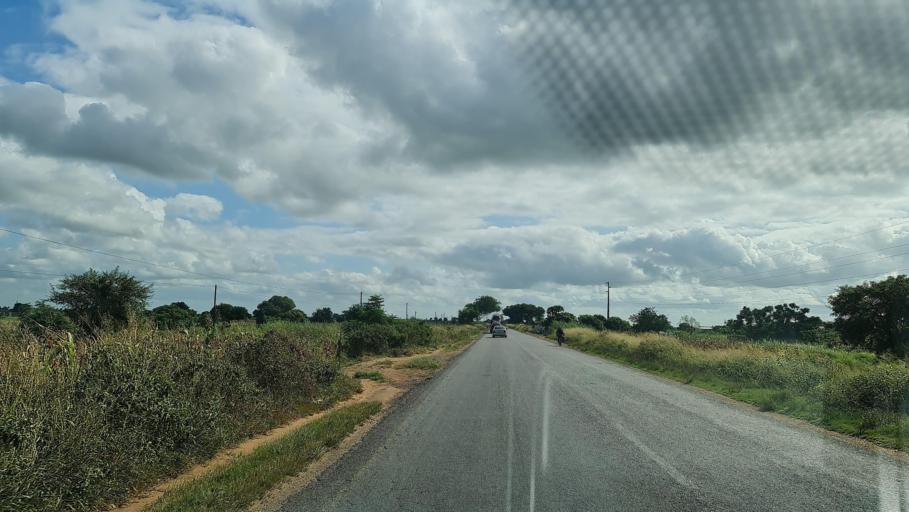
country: MZ
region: Gaza
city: Macia
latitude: -25.0833
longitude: 32.8471
